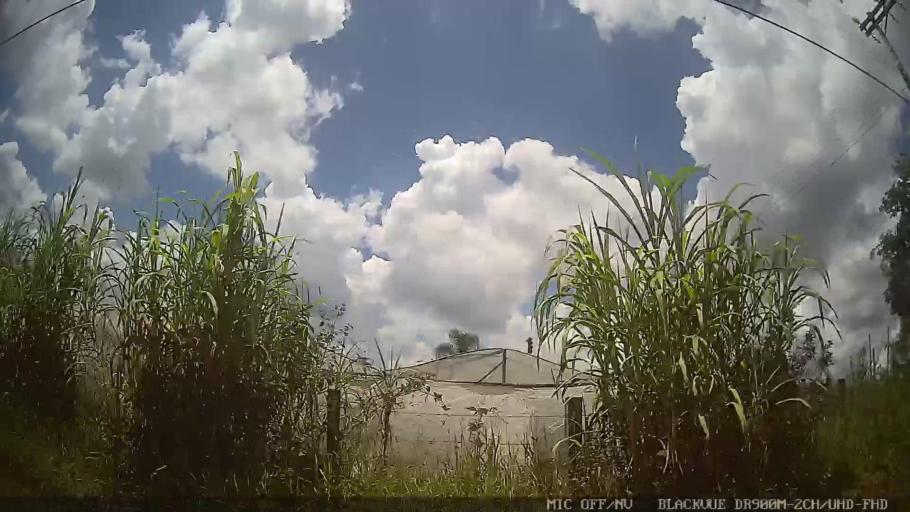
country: BR
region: Sao Paulo
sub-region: Jarinu
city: Jarinu
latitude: -23.1105
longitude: -46.6582
